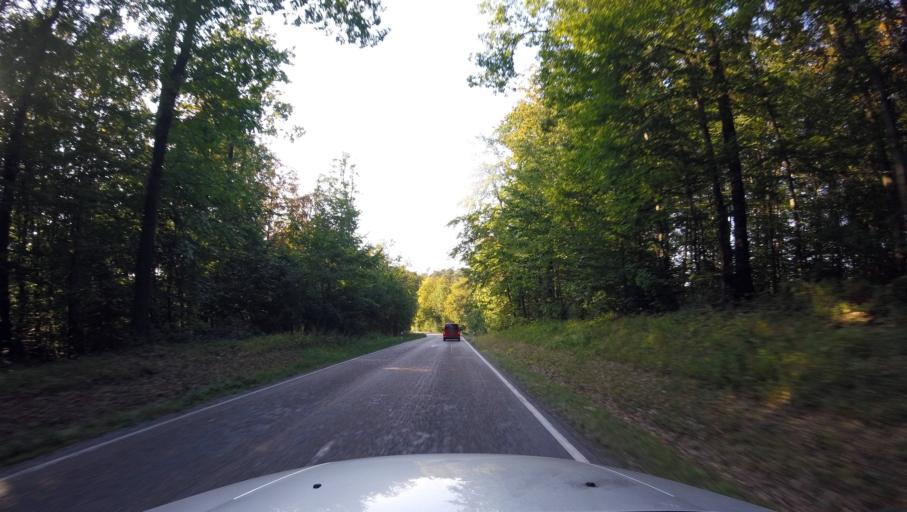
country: DE
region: Baden-Wuerttemberg
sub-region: Regierungsbezirk Stuttgart
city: Allmersbach im Tal
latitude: 48.8953
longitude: 9.4510
